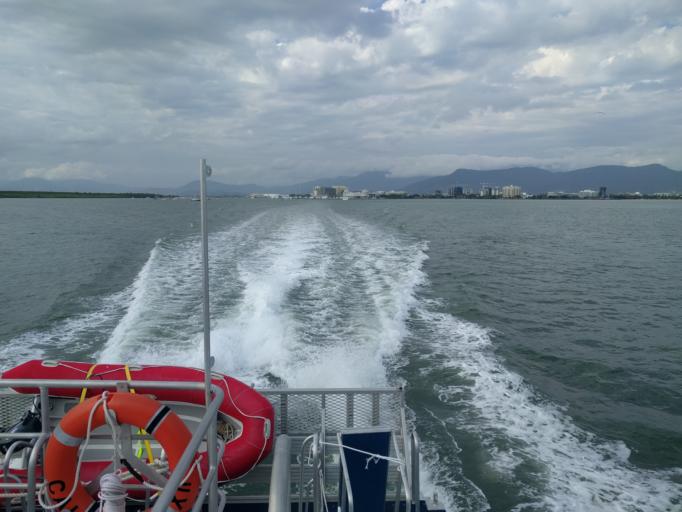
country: AU
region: Queensland
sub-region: Cairns
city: Cairns
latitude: -16.9058
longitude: 145.7888
